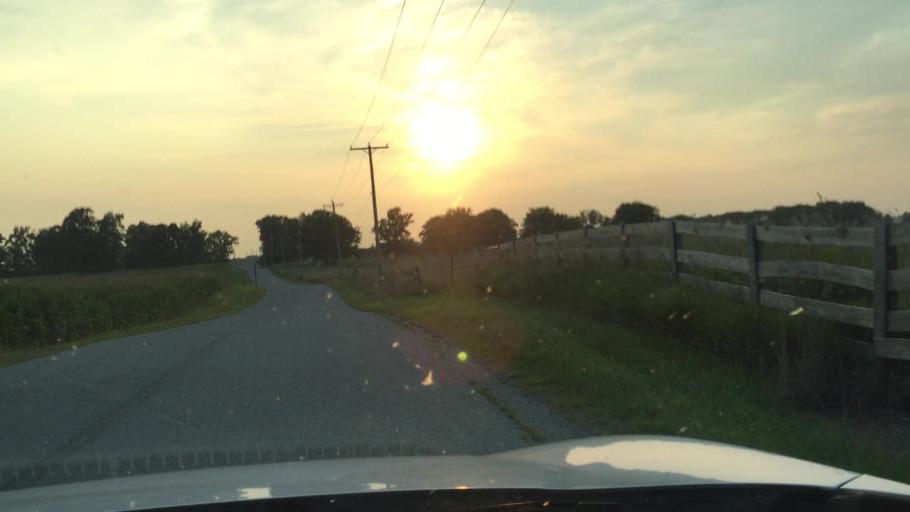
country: US
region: Ohio
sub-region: Madison County
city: Choctaw Lake
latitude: 39.9474
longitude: -83.5523
